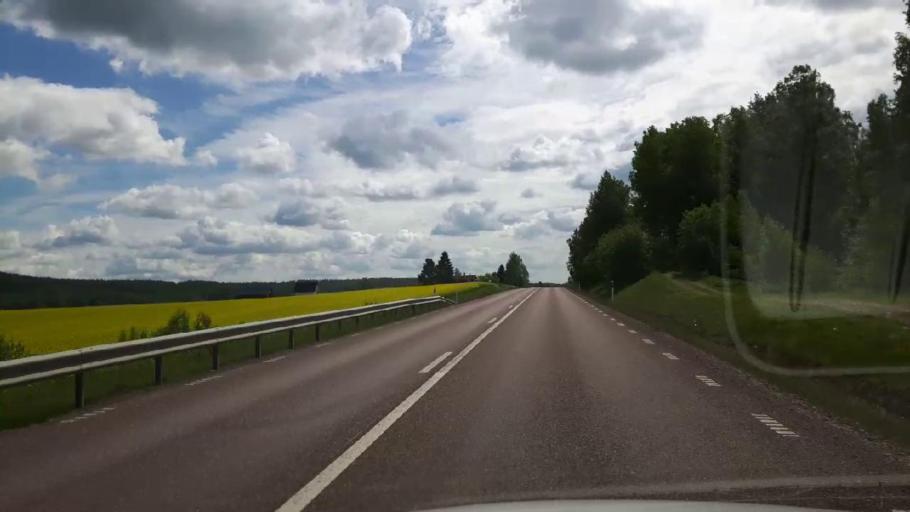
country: SE
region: Dalarna
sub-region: Hedemora Kommun
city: Hedemora
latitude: 60.3796
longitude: 15.9111
